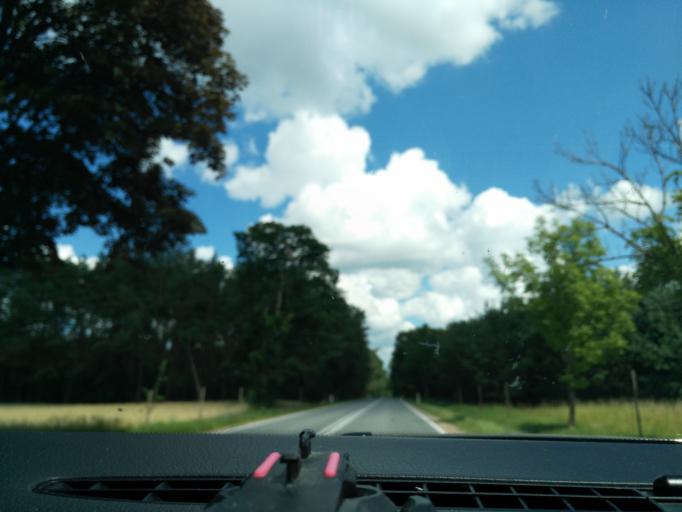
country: PL
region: Masovian Voivodeship
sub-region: Powiat losicki
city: Sarnaki
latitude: 52.3380
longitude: 22.8764
